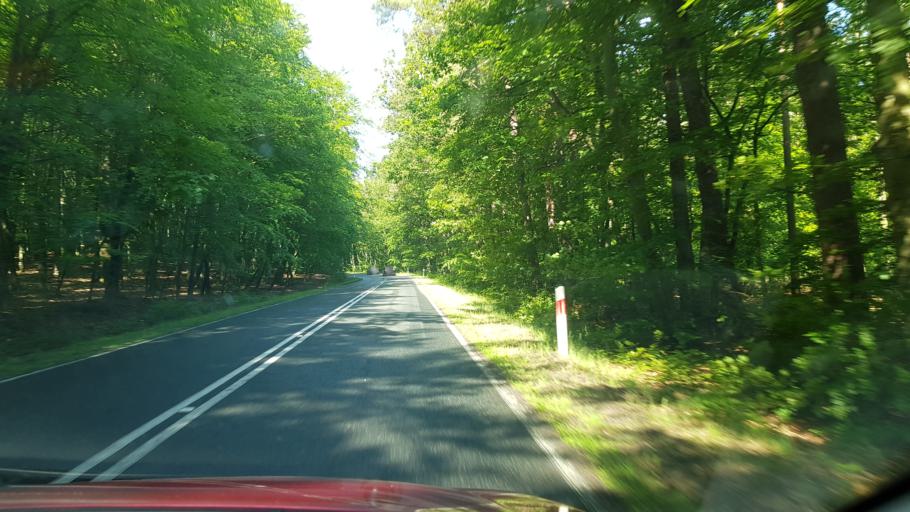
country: PL
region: West Pomeranian Voivodeship
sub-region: Powiat kamienski
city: Miedzyzdroje
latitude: 53.9595
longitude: 14.5092
